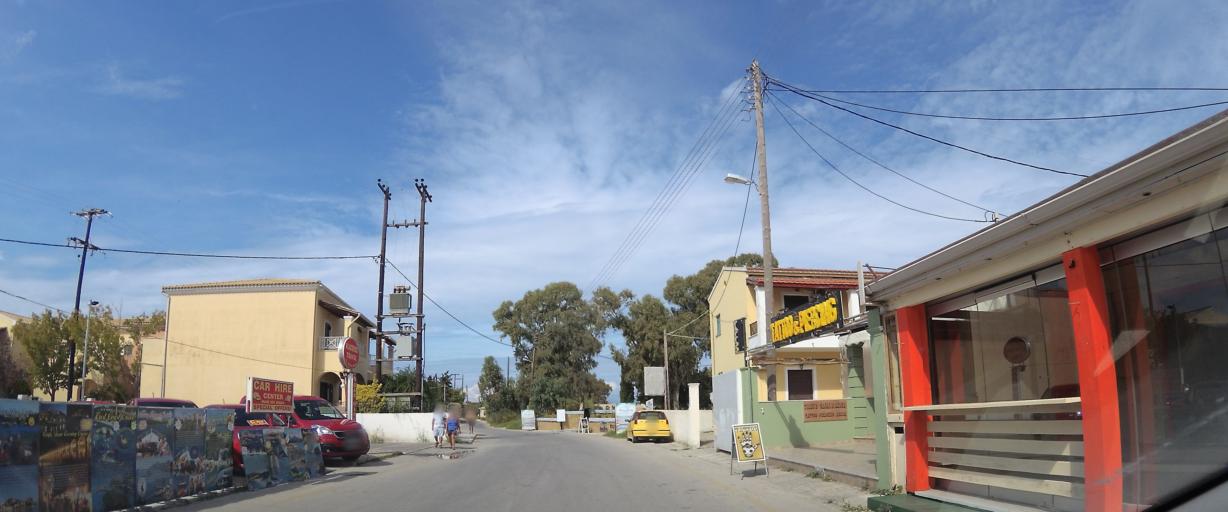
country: GR
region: Ionian Islands
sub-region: Nomos Kerkyras
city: Agios Georgis
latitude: 39.7927
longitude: 19.7024
